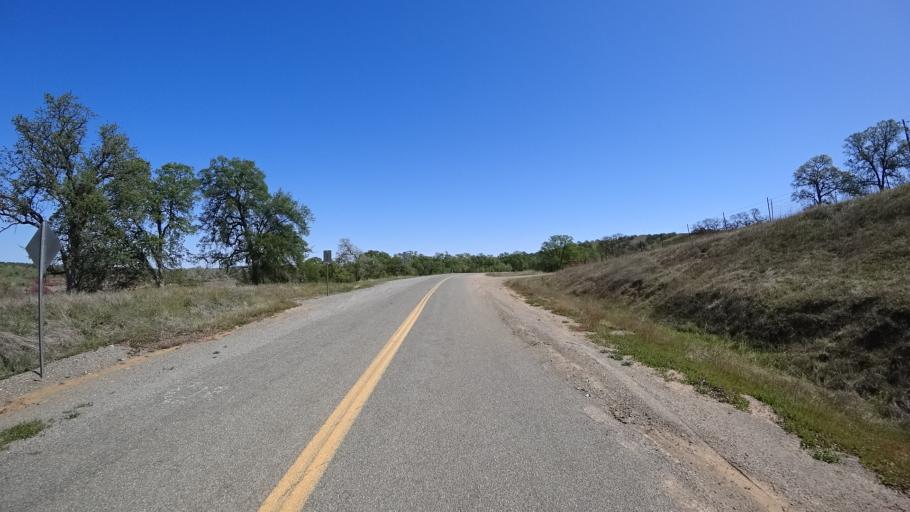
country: US
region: California
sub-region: Glenn County
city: Orland
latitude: 39.7314
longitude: -122.4122
